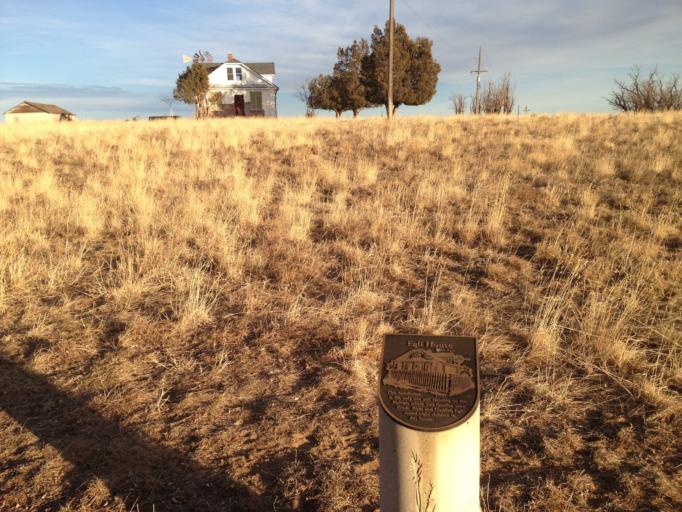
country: US
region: Colorado
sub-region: Adams County
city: Derby
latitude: 39.8218
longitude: -104.8632
